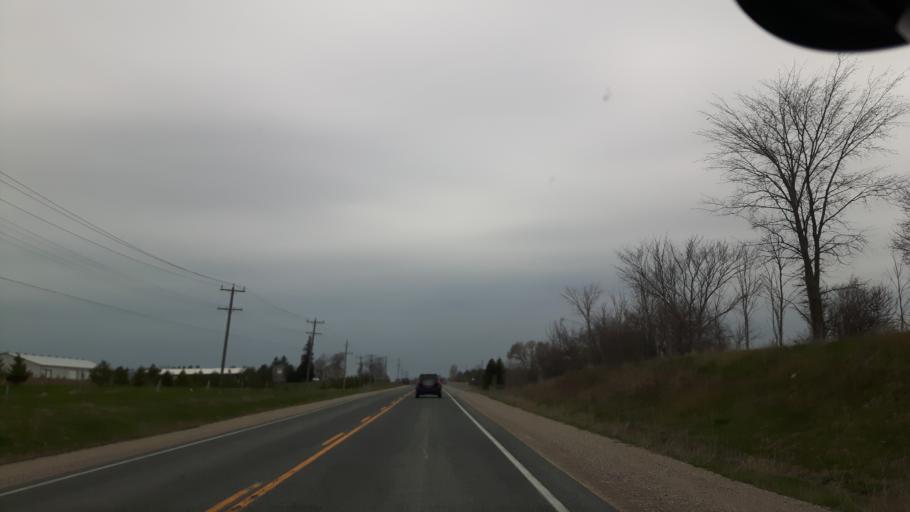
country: CA
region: Ontario
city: Goderich
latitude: 43.6814
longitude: -81.6286
